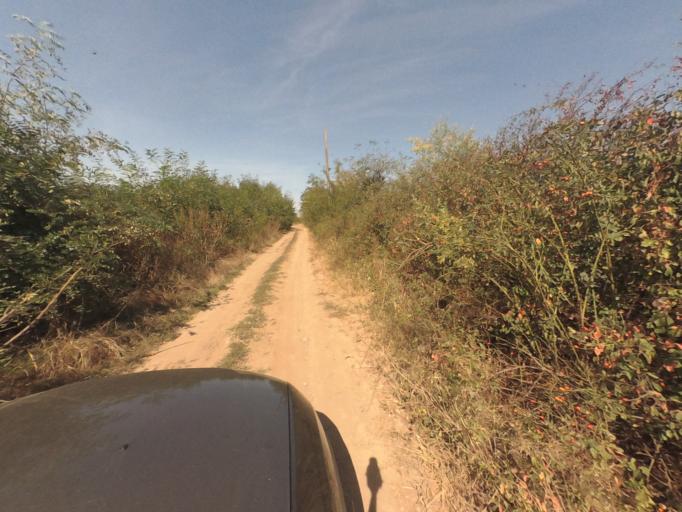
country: RO
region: Vaslui
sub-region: Comuna Costesti
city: Costesti
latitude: 46.5186
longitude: 27.7413
